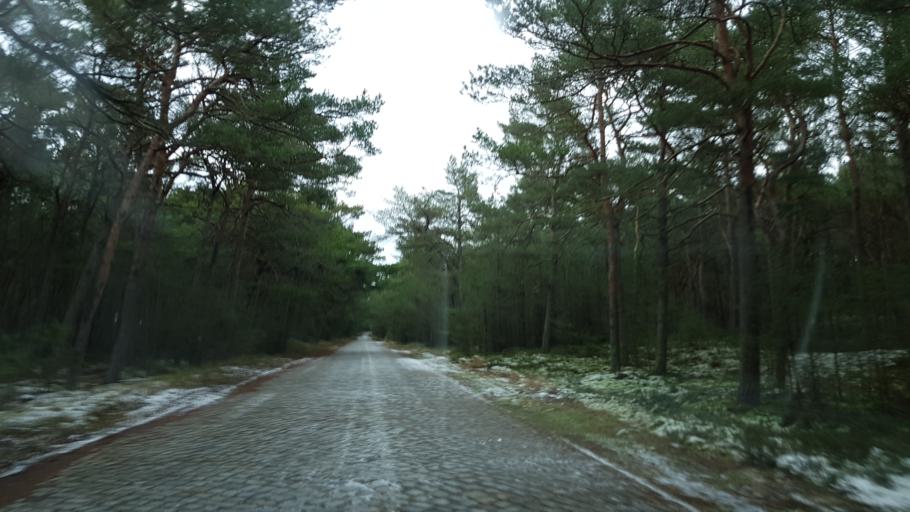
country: PL
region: West Pomeranian Voivodeship
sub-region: Powiat gryficki
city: Trzebiatow
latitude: 54.1214
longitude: 15.1955
